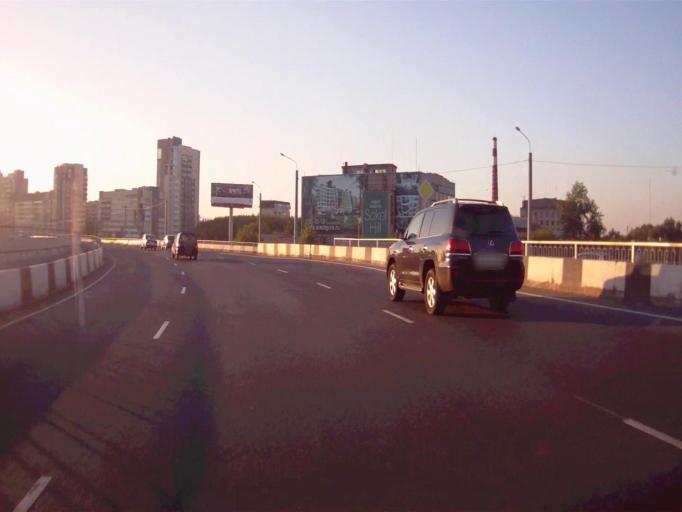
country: RU
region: Chelyabinsk
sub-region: Gorod Chelyabinsk
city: Chelyabinsk
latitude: 55.1722
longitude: 61.4120
